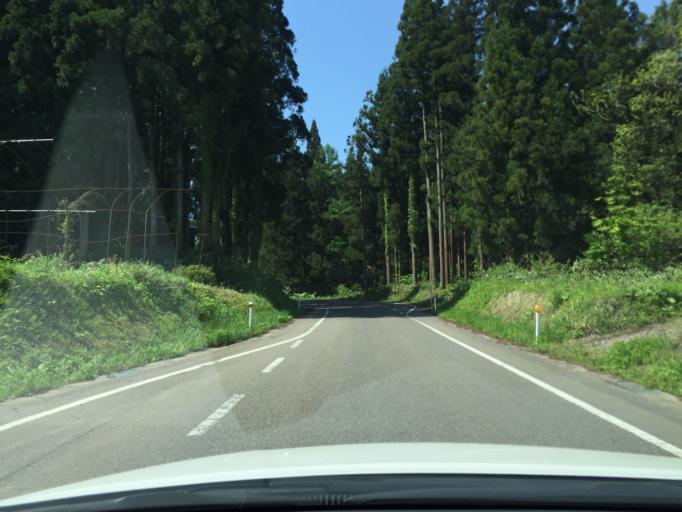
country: JP
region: Niigata
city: Kamo
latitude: 37.5745
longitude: 139.0862
